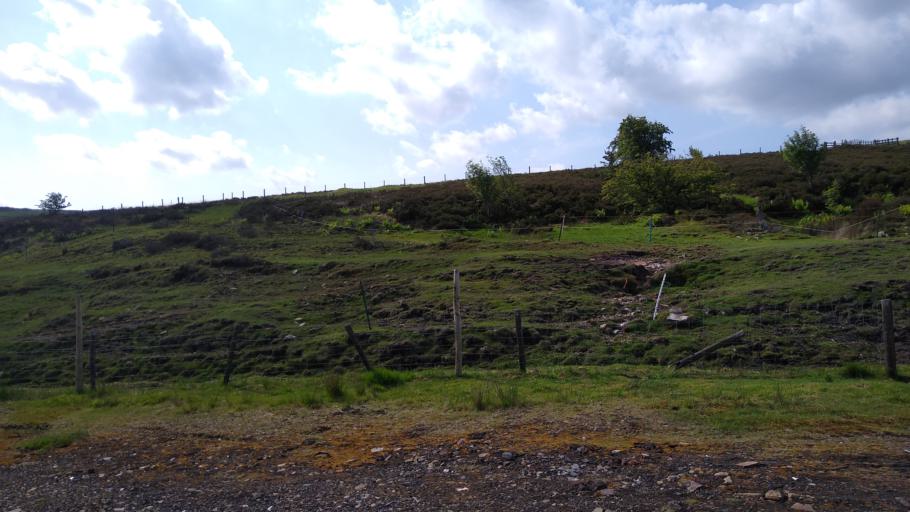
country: GB
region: England
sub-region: Northumberland
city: Greenhead
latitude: 54.9252
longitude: -2.5960
